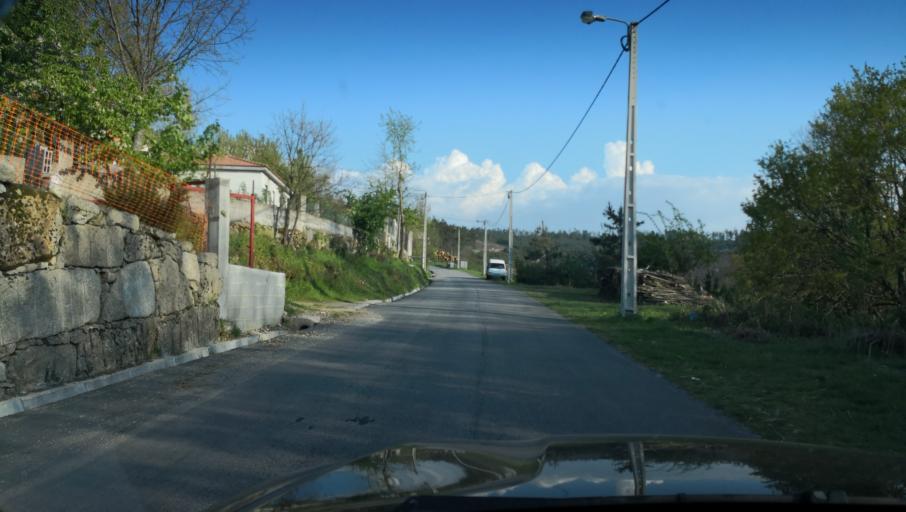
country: PT
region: Vila Real
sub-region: Santa Marta de Penaguiao
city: Santa Marta de Penaguiao
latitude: 41.2831
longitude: -7.8319
